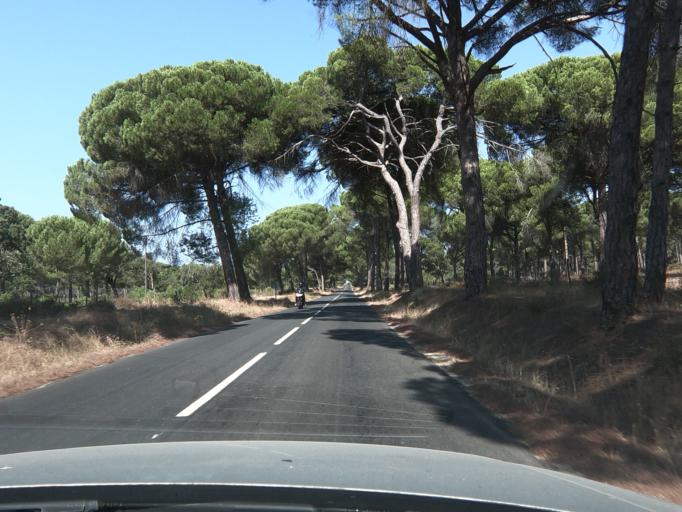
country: PT
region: Setubal
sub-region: Alcacer do Sal
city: Alcacer do Sal
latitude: 38.3259
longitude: -8.4395
